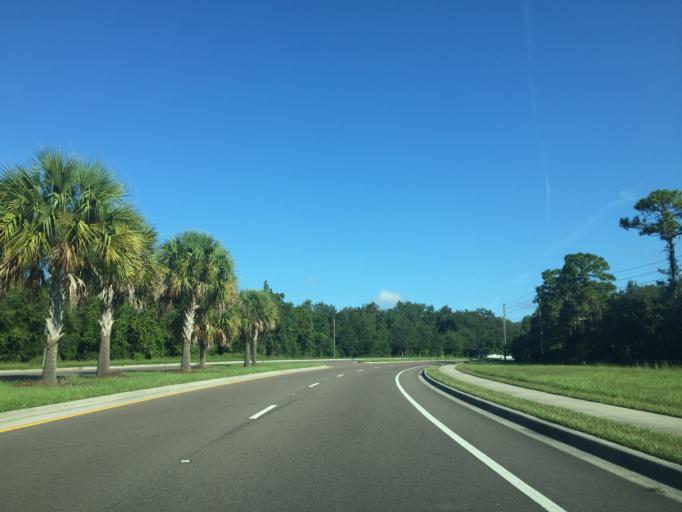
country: US
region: Florida
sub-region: Seminole County
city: Winter Springs
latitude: 28.6645
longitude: -81.2859
